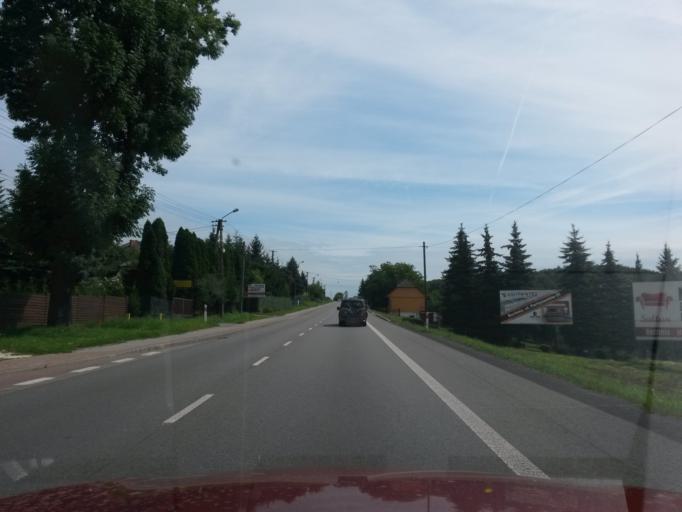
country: PL
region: Lesser Poland Voivodeship
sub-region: Powiat bochenski
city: Lapczyca
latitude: 49.9599
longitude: 20.3890
